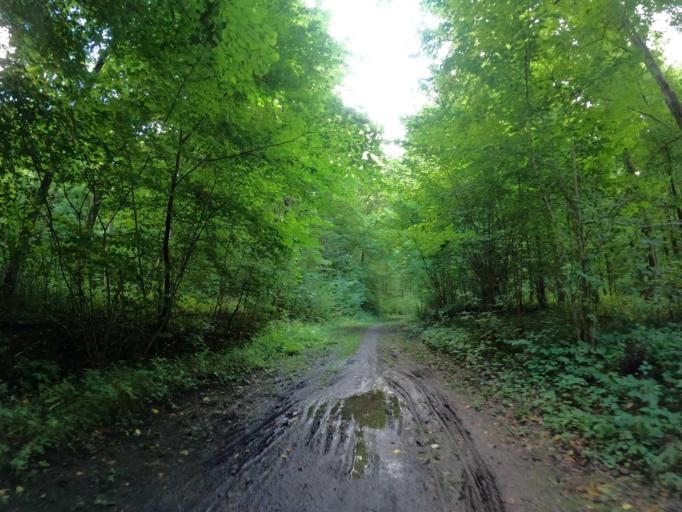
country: DE
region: Mecklenburg-Vorpommern
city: Putbus
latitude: 54.3614
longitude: 13.4353
